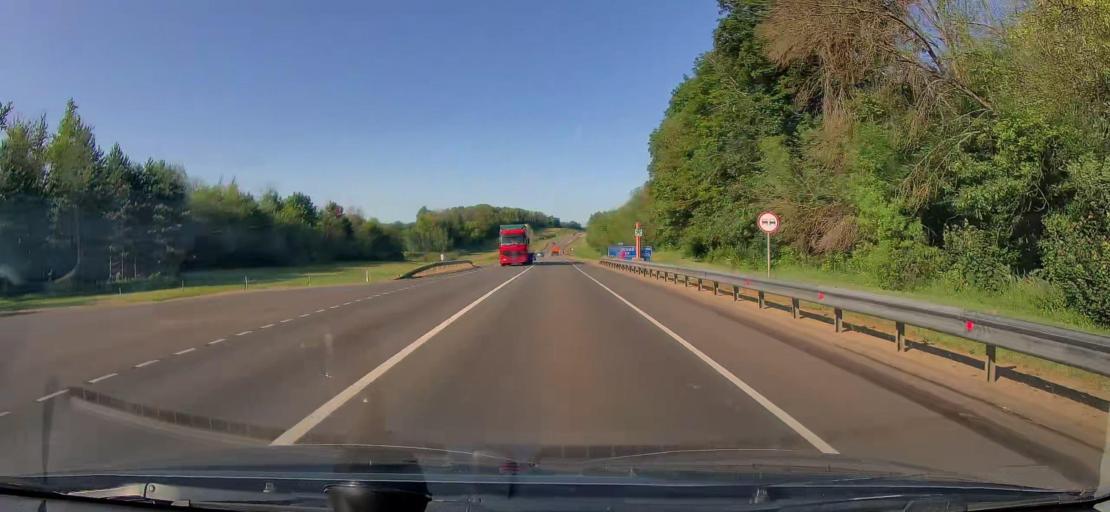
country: RU
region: Orjol
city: Mtsensk
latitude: 53.1274
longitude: 36.3297
